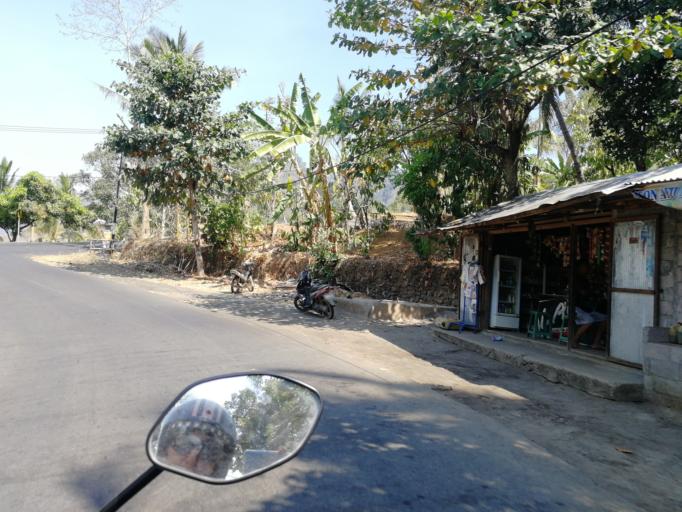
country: ID
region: Bali
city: Banjar Kedisan
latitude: -8.1408
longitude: 115.3157
